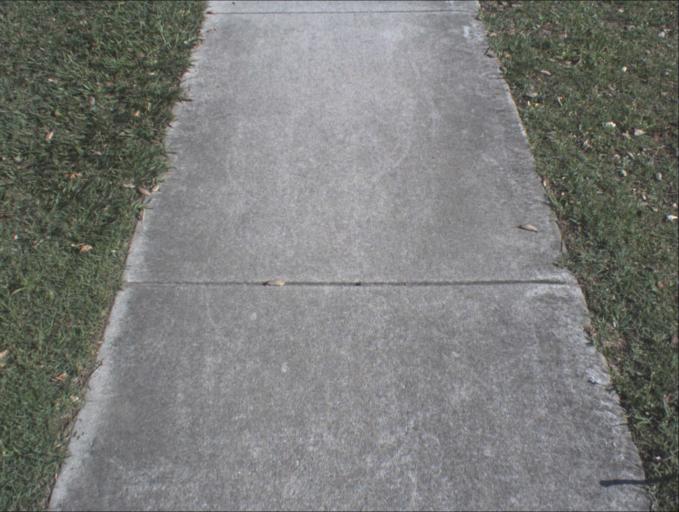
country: AU
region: Queensland
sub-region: Logan
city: Logan Reserve
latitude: -27.6974
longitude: 153.0848
